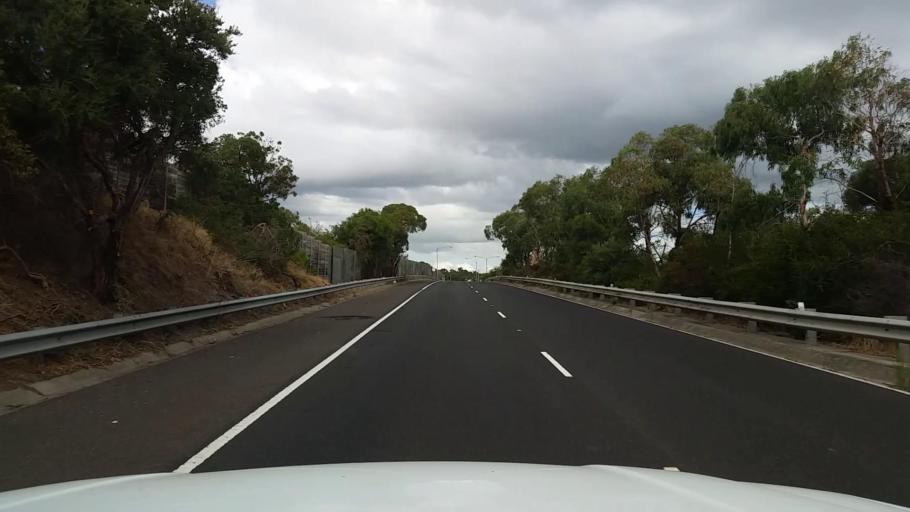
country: AU
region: Victoria
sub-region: Frankston
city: Frankston East
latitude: -38.1420
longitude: 145.1367
